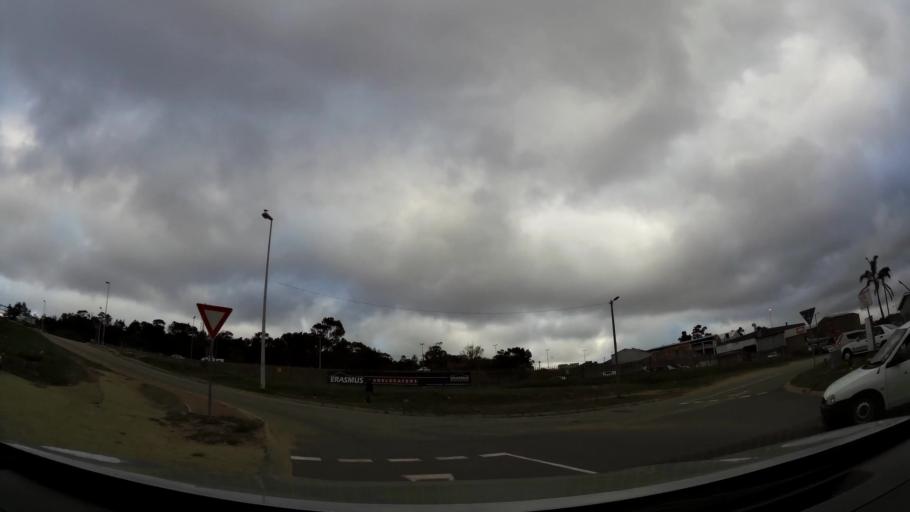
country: ZA
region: Western Cape
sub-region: Eden District Municipality
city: Plettenberg Bay
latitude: -34.0495
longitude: 23.3563
